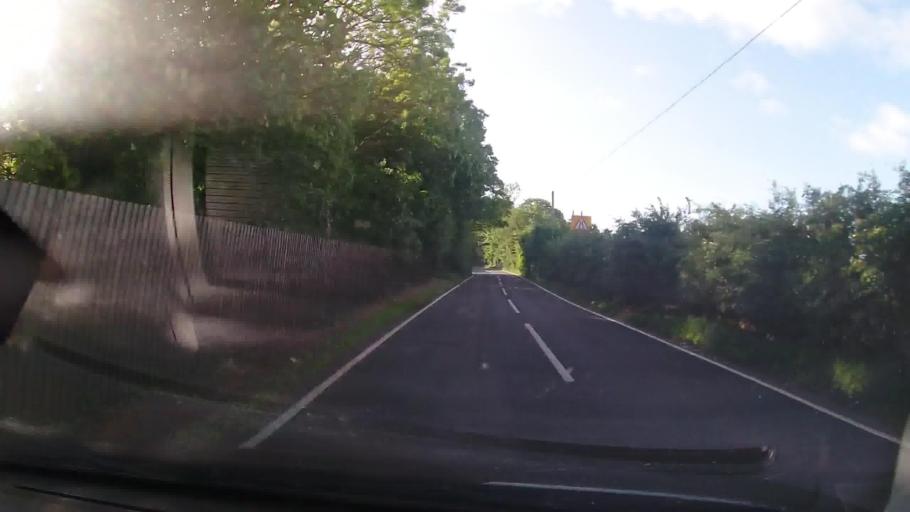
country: GB
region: England
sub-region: Shropshire
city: Wem
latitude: 52.8415
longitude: -2.7110
